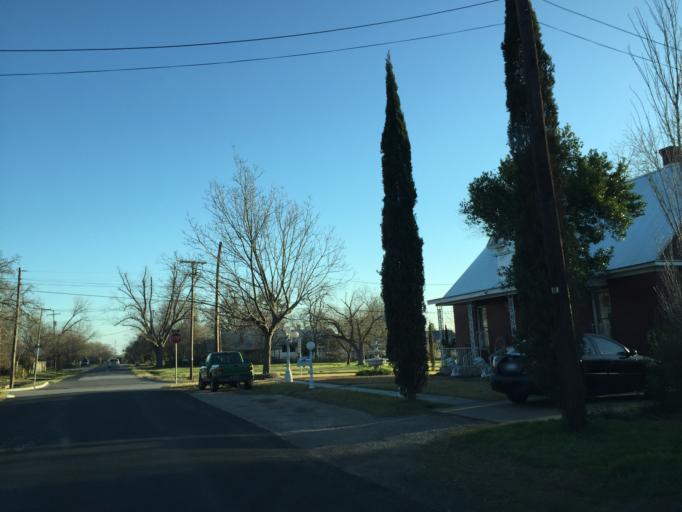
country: US
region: Texas
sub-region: Bastrop County
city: Elgin
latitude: 30.3489
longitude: -97.3743
